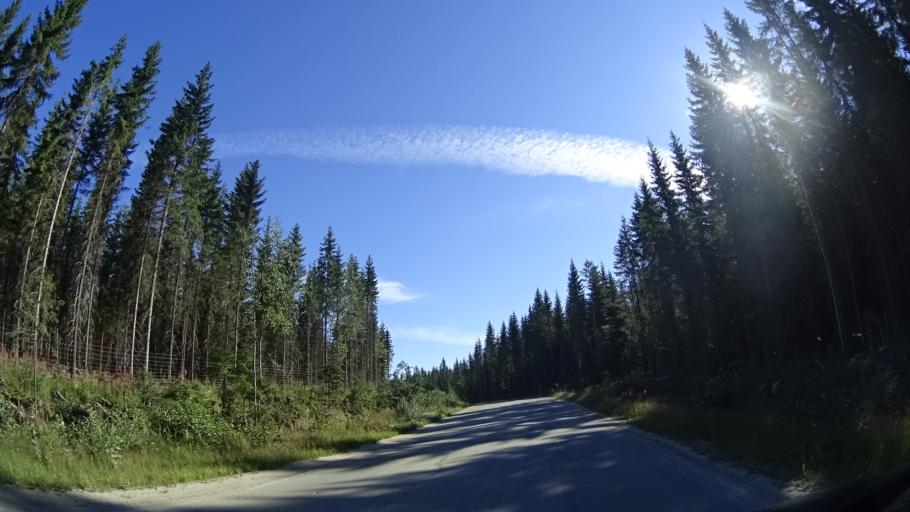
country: FI
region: Central Finland
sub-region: Jyvaeskylae
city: Petaejaevesi
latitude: 62.3060
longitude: 25.3377
